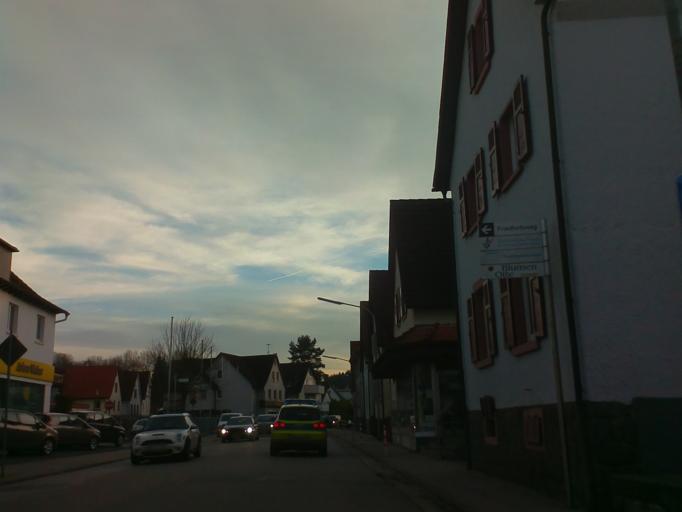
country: DE
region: Hesse
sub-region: Regierungsbezirk Darmstadt
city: Rimbach
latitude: 49.6216
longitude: 8.7587
